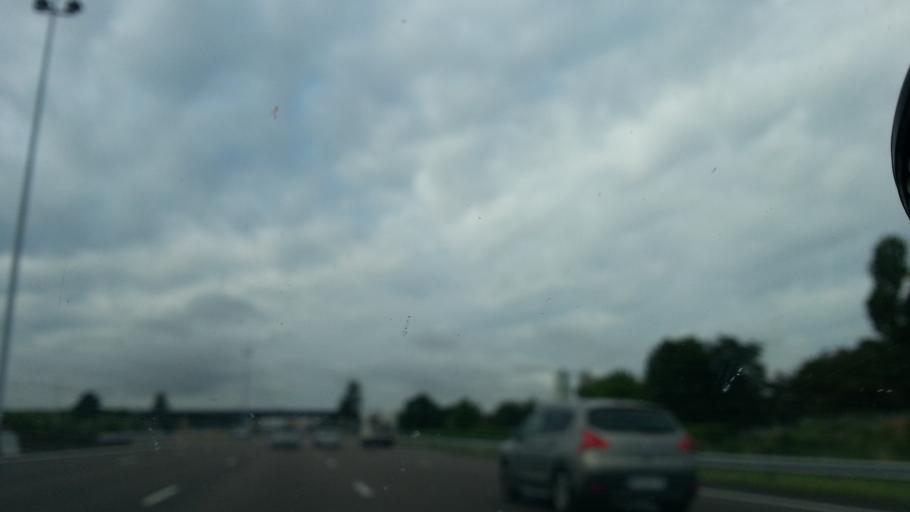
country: FR
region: Bourgogne
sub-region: Departement de la Cote-d'Or
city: Beaune
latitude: 47.0198
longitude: 4.8699
